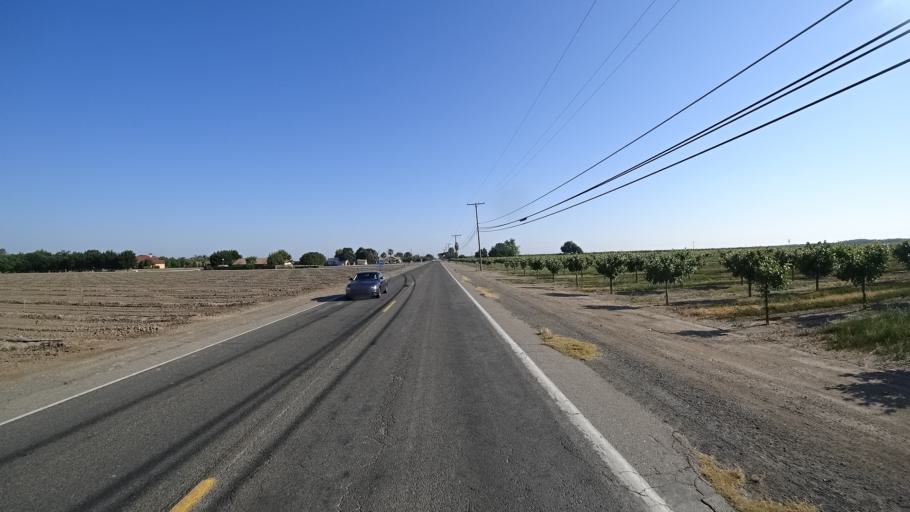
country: US
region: California
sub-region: Kings County
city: Armona
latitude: 36.3540
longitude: -119.7090
